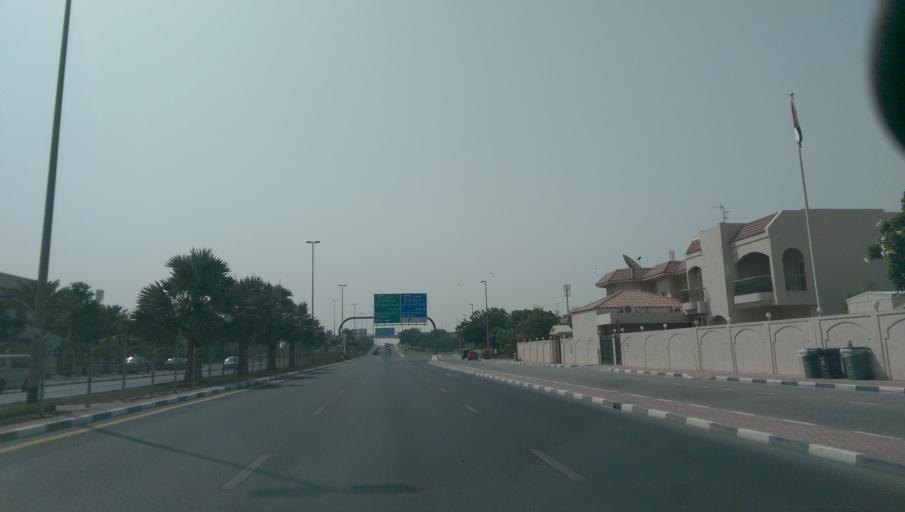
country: AE
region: Dubai
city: Dubai
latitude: 25.1519
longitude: 55.2200
